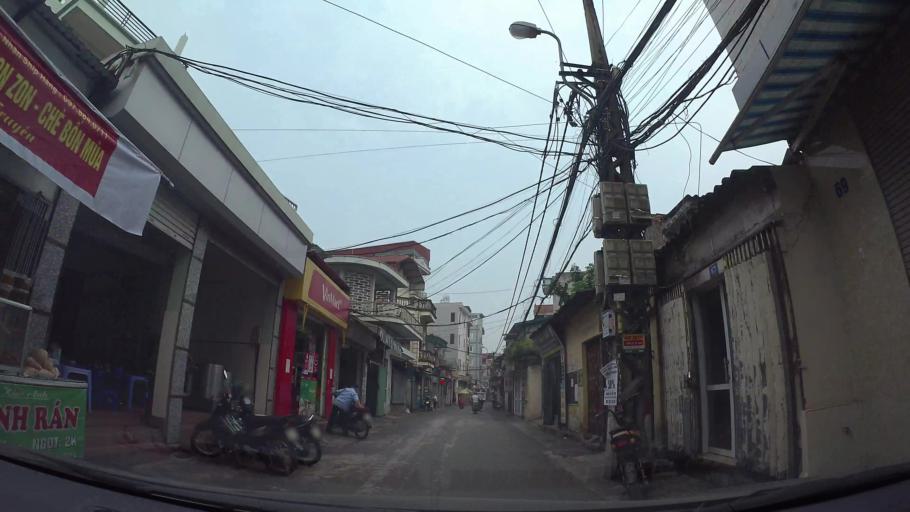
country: VN
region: Ha Noi
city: Van Dien
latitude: 20.9723
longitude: 105.8684
